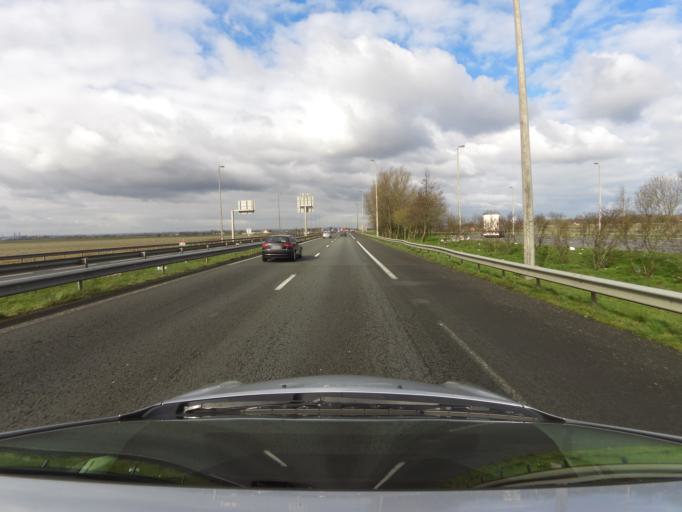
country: FR
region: Nord-Pas-de-Calais
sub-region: Departement du Pas-de-Calais
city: Marck
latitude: 50.9376
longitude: 1.9367
